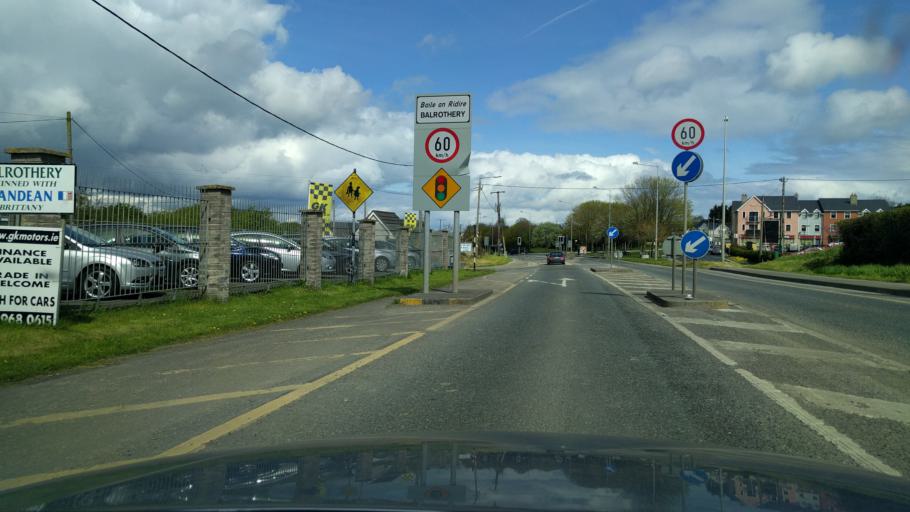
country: IE
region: Leinster
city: Balrothery
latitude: 53.5869
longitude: -6.1906
